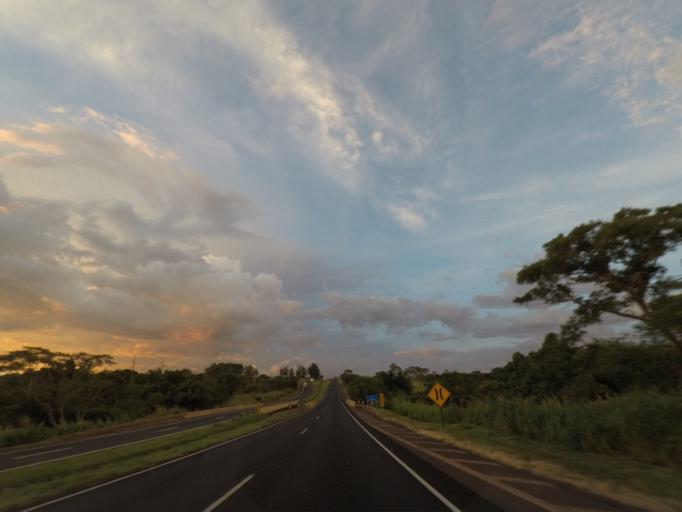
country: BR
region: Minas Gerais
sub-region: Uberaba
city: Uberaba
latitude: -19.6094
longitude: -48.0216
